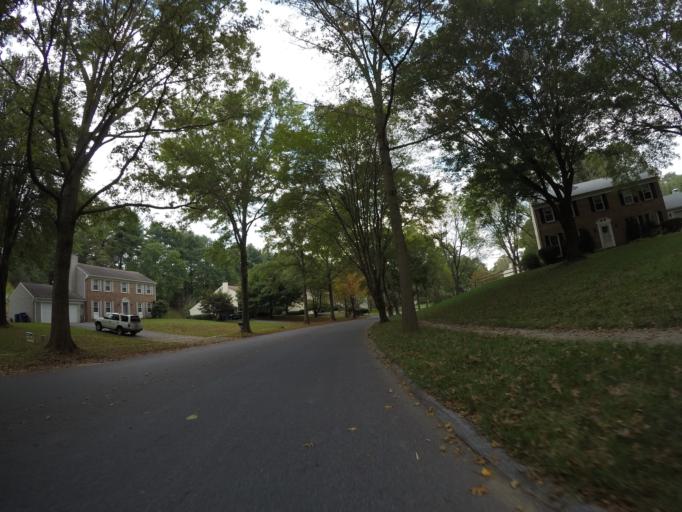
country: US
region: Maryland
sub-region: Howard County
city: Columbia
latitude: 39.2694
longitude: -76.8608
